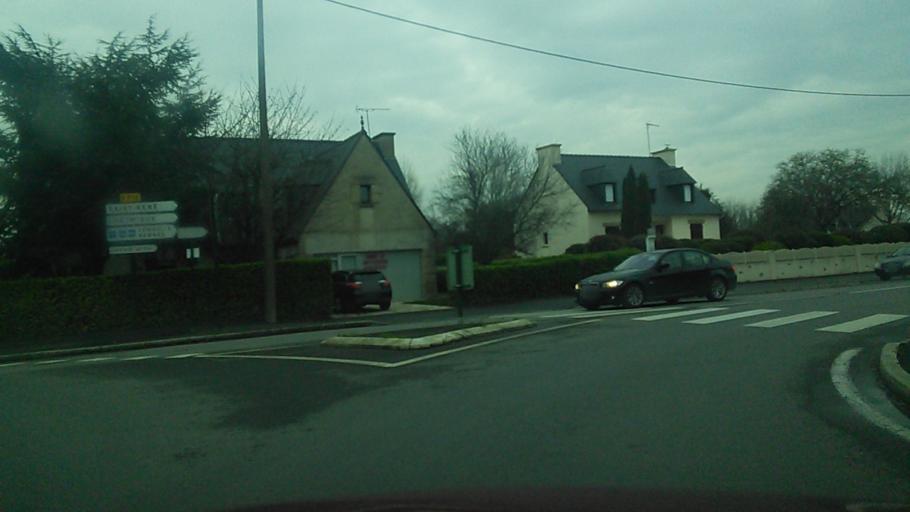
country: FR
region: Brittany
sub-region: Departement des Cotes-d'Armor
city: Pommeret
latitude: 48.4848
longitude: -2.6442
